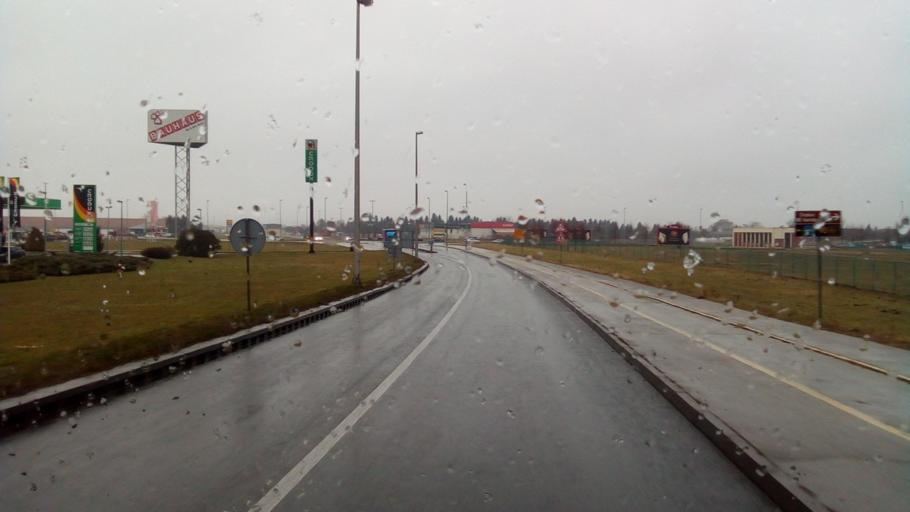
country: HR
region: Varazdinska
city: Varazdin
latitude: 46.2934
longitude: 16.3513
